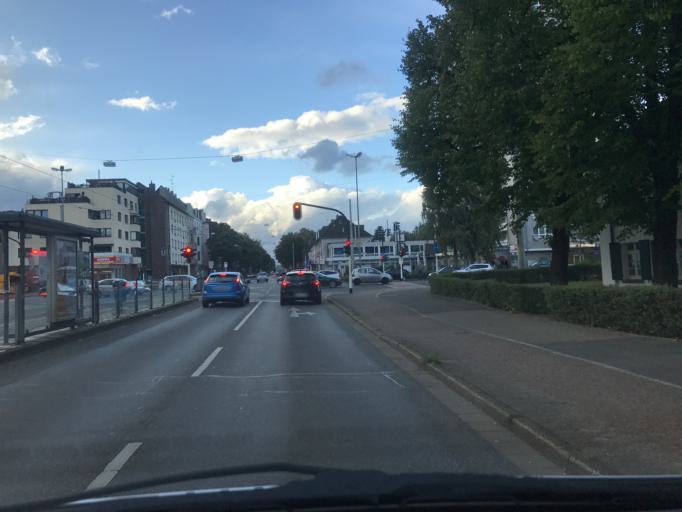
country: DE
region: North Rhine-Westphalia
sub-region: Regierungsbezirk Dusseldorf
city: Krefeld
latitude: 51.3162
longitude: 6.5767
